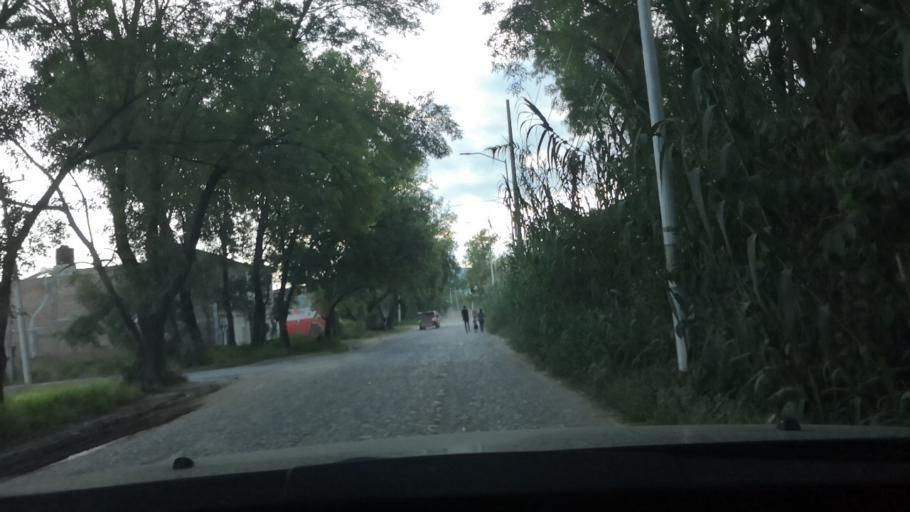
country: MX
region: Guanajuato
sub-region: San Francisco del Rincon
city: Fraccionamiento la Mezquitera
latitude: 21.0209
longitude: -101.8419
